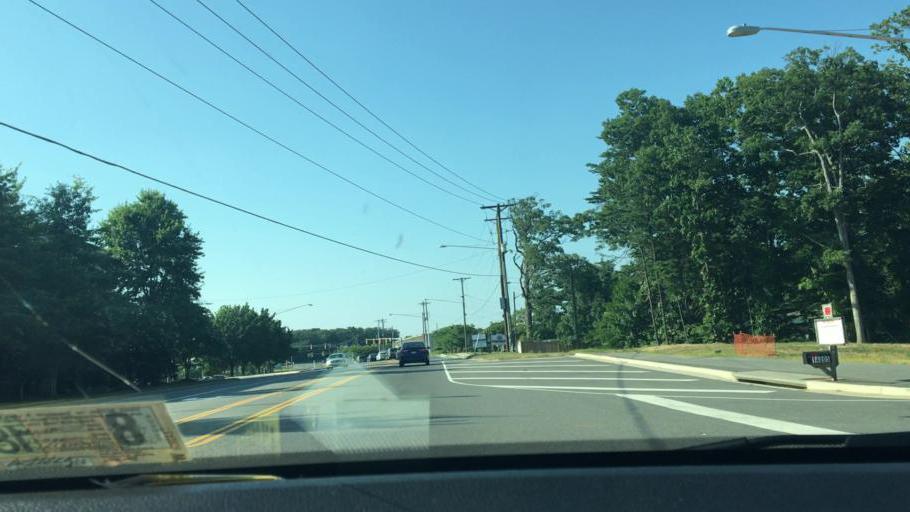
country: US
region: Virginia
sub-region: Prince William County
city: Potomac Mills
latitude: 38.6488
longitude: -77.2898
